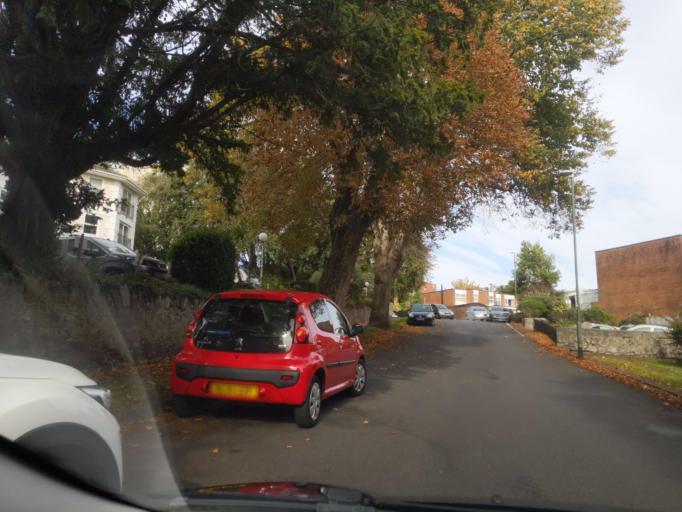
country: GB
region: England
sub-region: Borough of Torbay
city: Torquay
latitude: 50.4685
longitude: -3.5041
